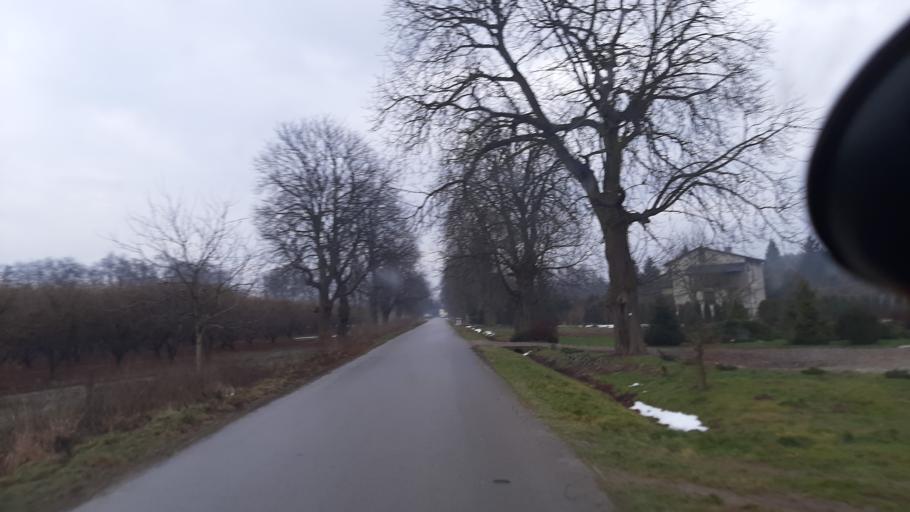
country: PL
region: Lublin Voivodeship
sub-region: Powiat lubelski
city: Lublin
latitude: 51.3349
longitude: 22.5495
